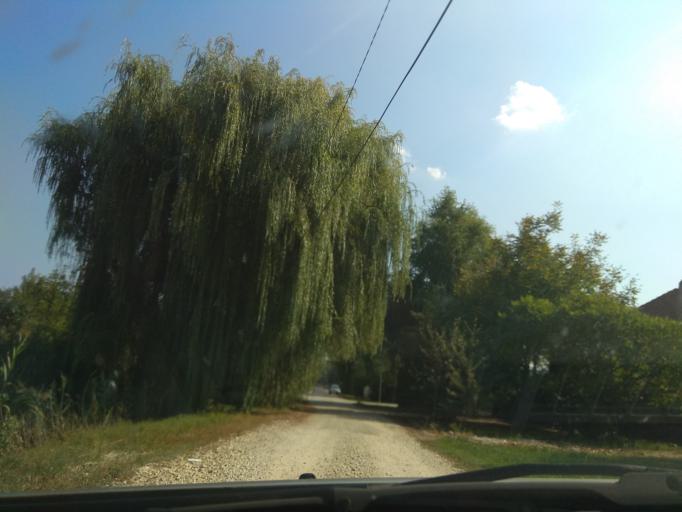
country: HU
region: Borsod-Abauj-Zemplen
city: Miskolc
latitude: 48.0749
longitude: 20.7693
